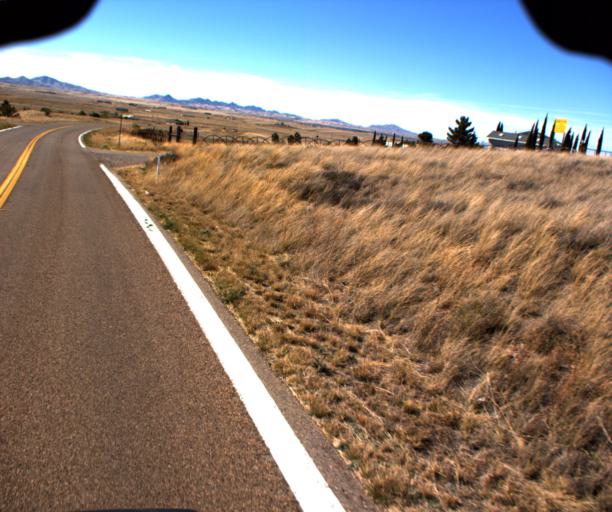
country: US
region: Arizona
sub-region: Cochise County
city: Huachuca City
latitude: 31.6682
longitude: -110.6063
